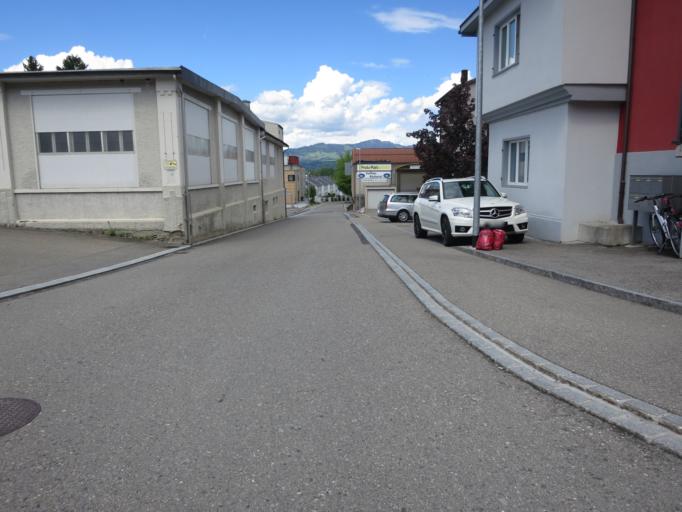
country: CH
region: Schwyz
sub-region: Bezirk March
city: Reichenburg
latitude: 47.1734
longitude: 8.9569
